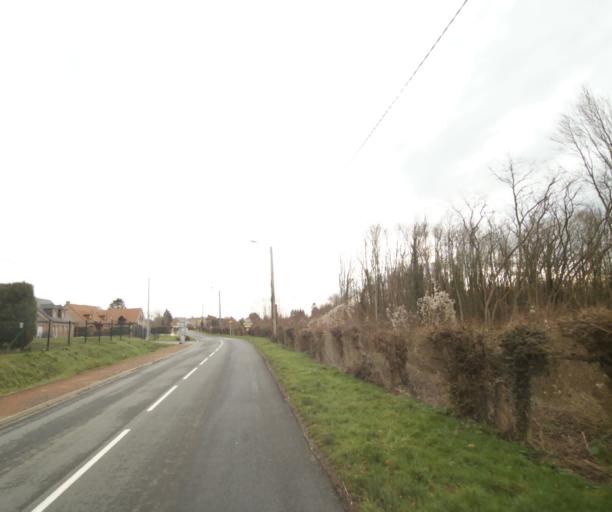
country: FR
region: Nord-Pas-de-Calais
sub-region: Departement du Nord
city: Sebourg
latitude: 50.3311
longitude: 3.6608
